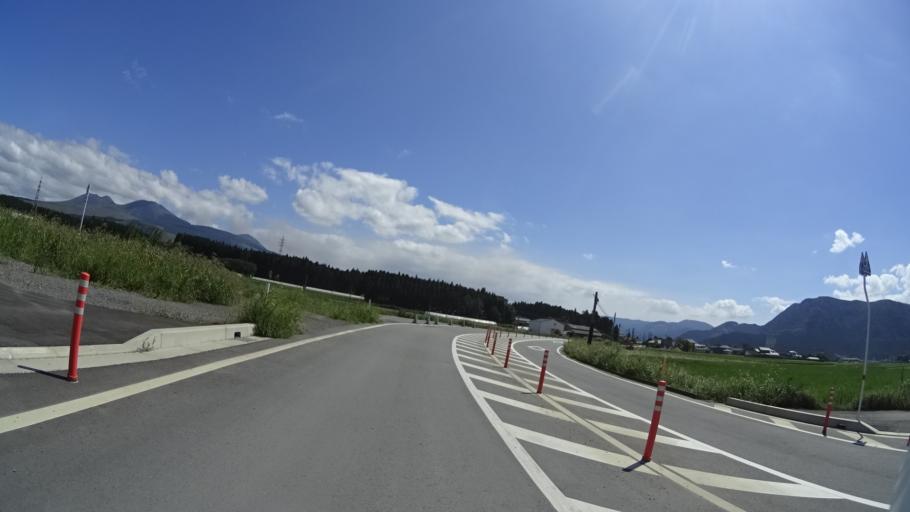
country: JP
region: Kumamoto
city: Aso
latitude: 32.9236
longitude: 130.9943
